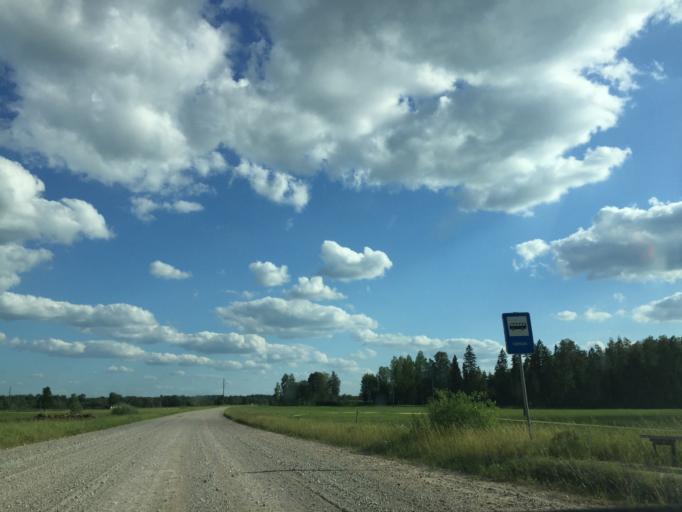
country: LV
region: Kandava
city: Kandava
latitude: 56.9064
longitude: 22.7926
